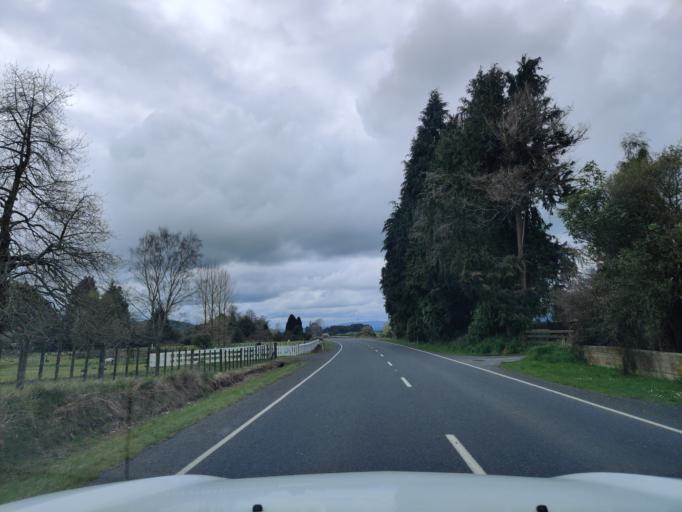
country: NZ
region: Waikato
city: Turangi
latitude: -38.9924
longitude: 175.3788
